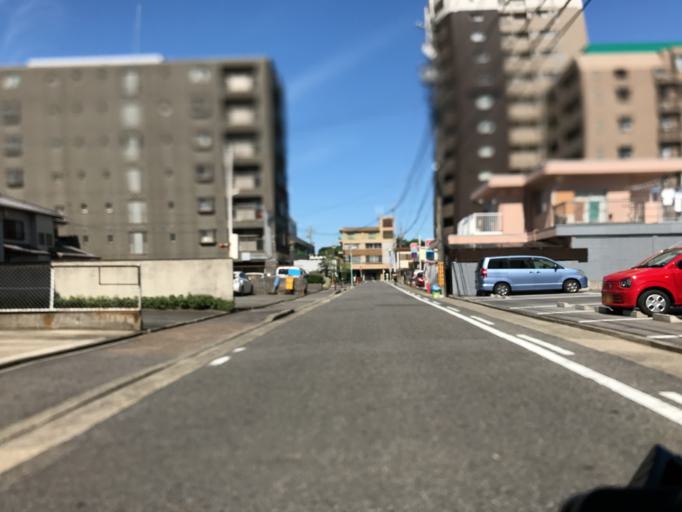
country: JP
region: Aichi
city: Nagoya-shi
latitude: 35.1791
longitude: 136.9127
